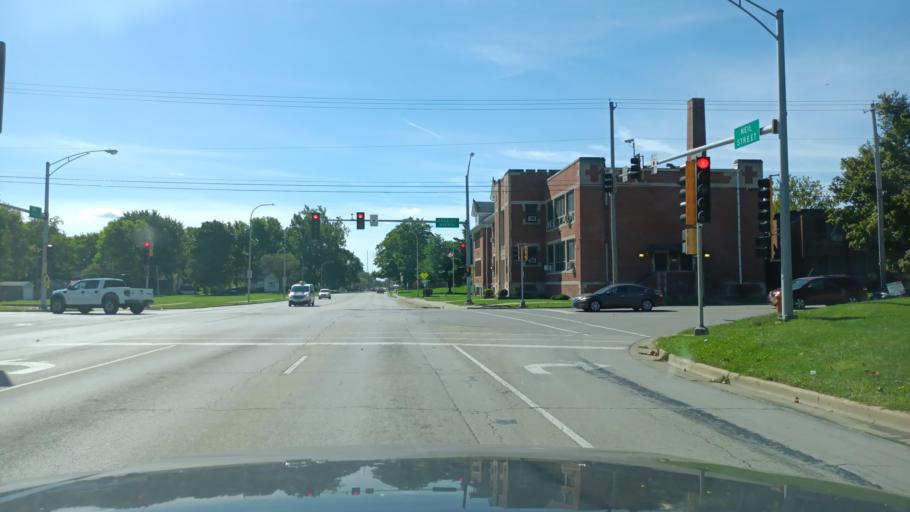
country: US
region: Illinois
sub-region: Champaign County
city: Champaign
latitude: 40.1276
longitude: -88.2437
